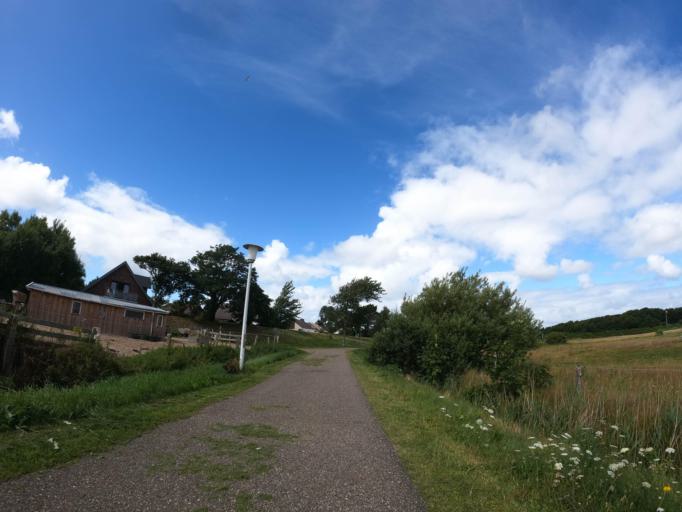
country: DE
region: Schleswig-Holstein
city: Westerland
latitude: 54.8964
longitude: 8.3141
